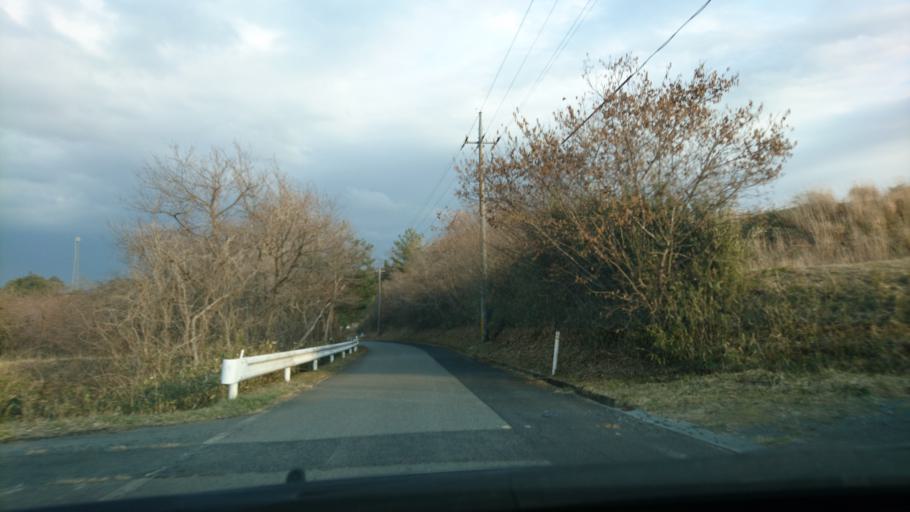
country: JP
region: Iwate
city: Ichinoseki
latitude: 38.8939
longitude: 141.2387
